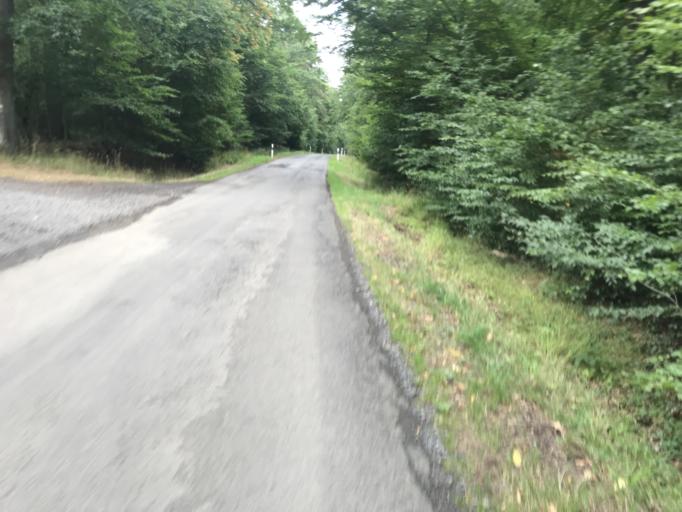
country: DE
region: Hesse
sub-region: Regierungsbezirk Giessen
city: Lohra
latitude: 50.6699
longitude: 8.6250
